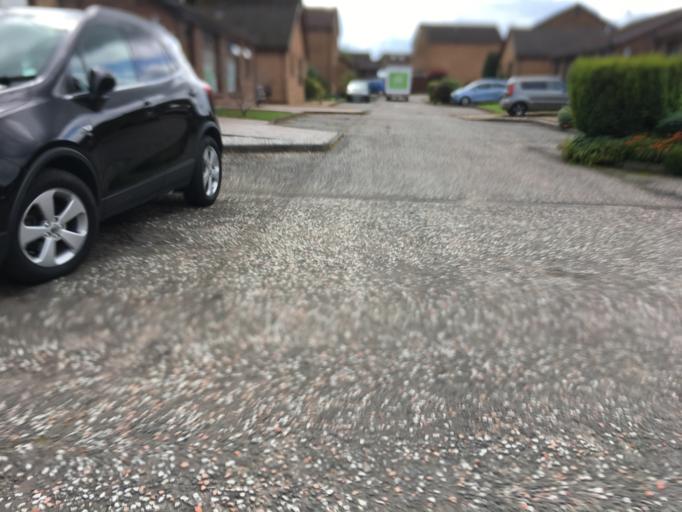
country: GB
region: Scotland
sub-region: West Lothian
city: Mid Calder
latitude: 55.8732
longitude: -3.5040
